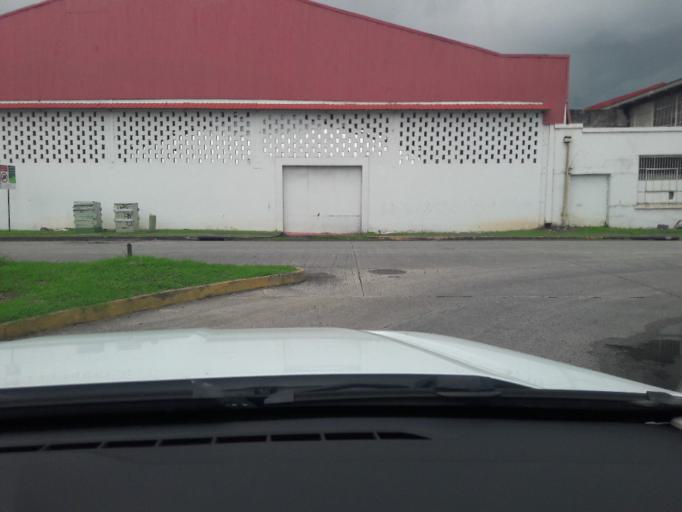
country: PA
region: Panama
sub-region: Distrito de Panama
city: Ancon
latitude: 8.9728
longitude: -79.5595
